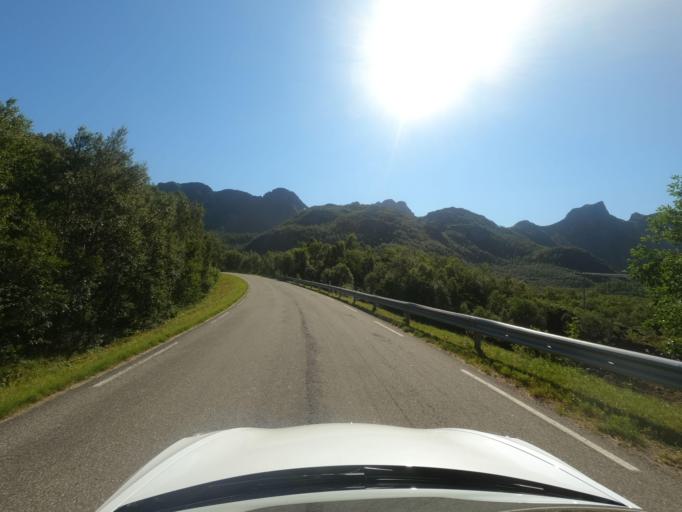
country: NO
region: Nordland
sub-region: Hadsel
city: Stokmarknes
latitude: 68.3570
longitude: 15.0637
